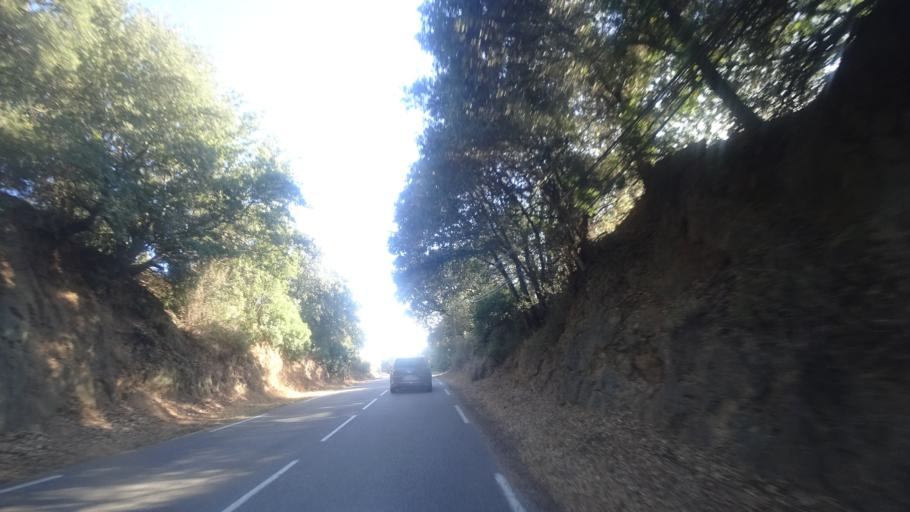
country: FR
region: Corsica
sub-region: Departement de la Corse-du-Sud
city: Cargese
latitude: 42.1619
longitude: 8.5975
